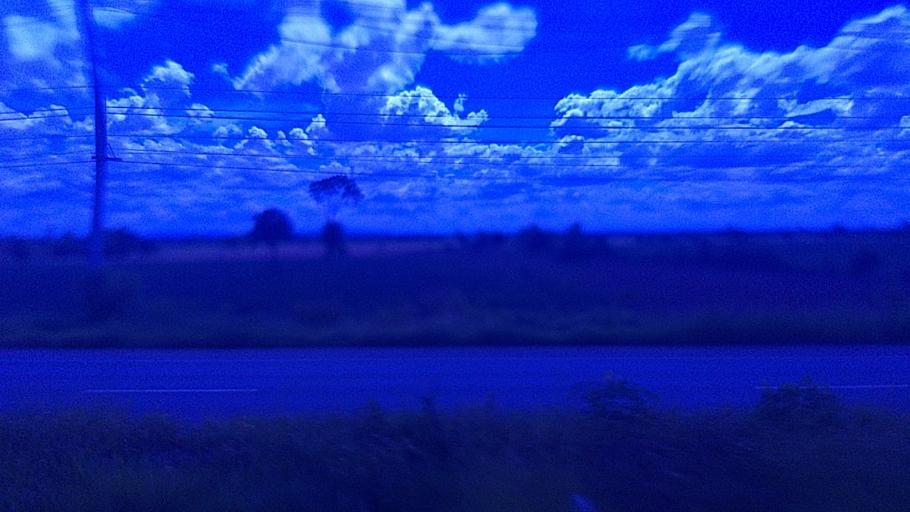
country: TH
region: Nakhon Ratchasima
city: Dan Khun Thot
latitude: 15.0986
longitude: 101.7210
